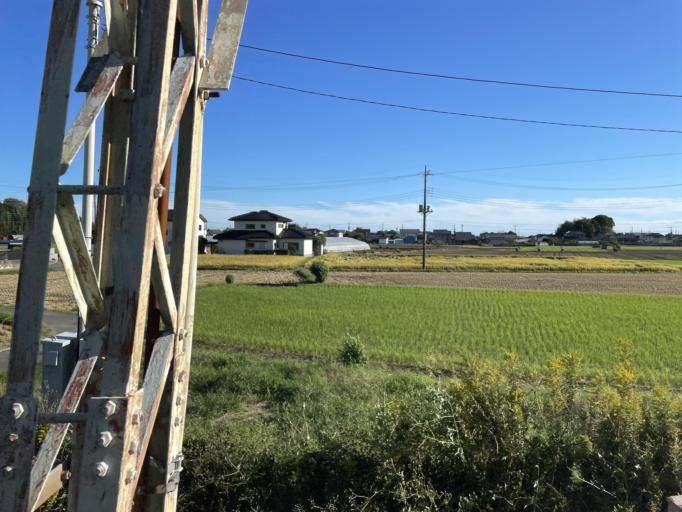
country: JP
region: Tochigi
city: Mibu
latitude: 36.4071
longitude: 139.7688
